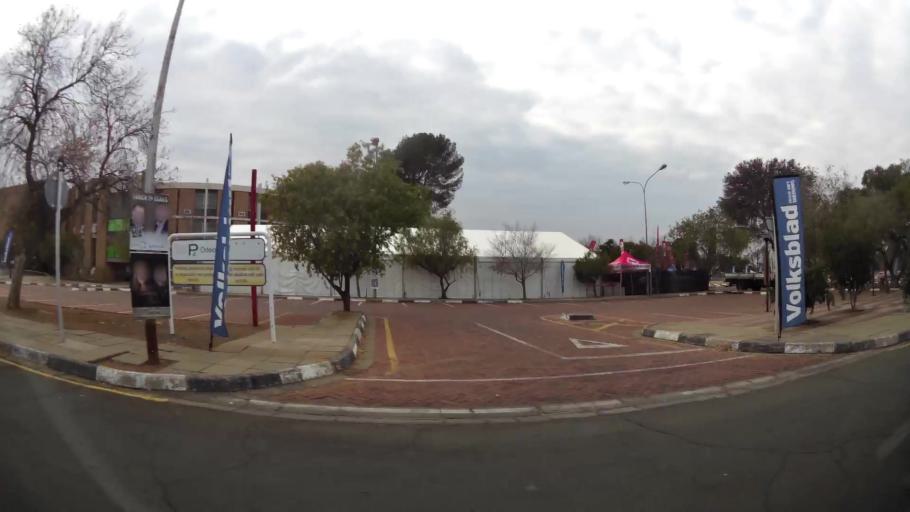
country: ZA
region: Orange Free State
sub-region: Mangaung Metropolitan Municipality
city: Bloemfontein
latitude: -29.1113
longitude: 26.1903
